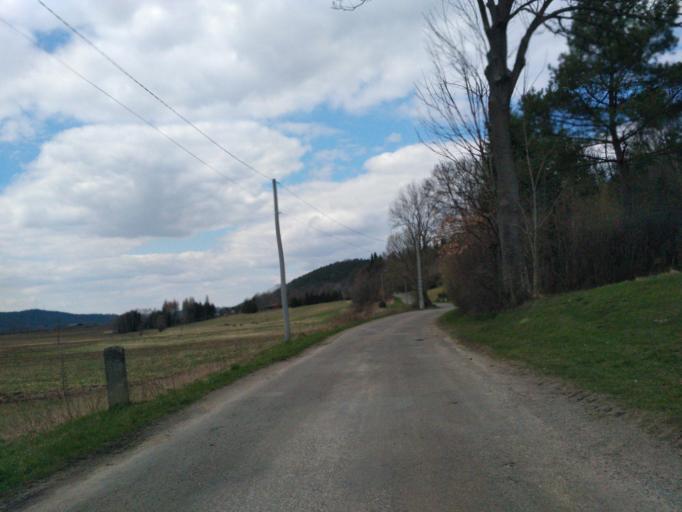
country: PL
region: Subcarpathian Voivodeship
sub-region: Powiat brzozowski
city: Dydnia
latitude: 49.6671
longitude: 22.2884
